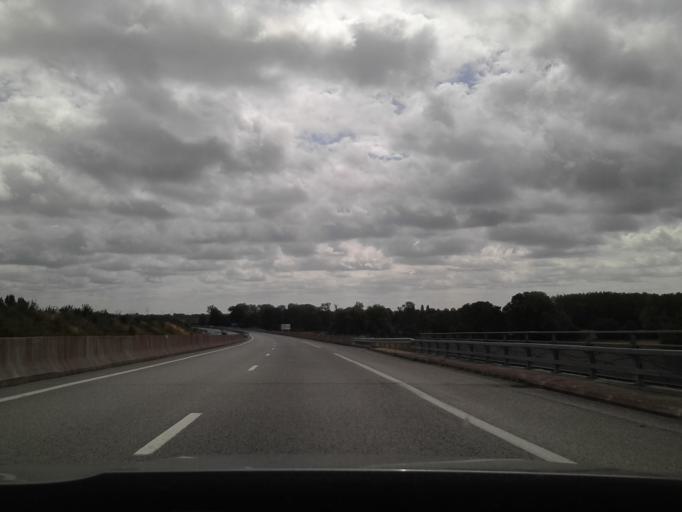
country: FR
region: Lower Normandy
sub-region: Departement de l'Orne
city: Mortree
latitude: 48.6571
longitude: 0.0871
